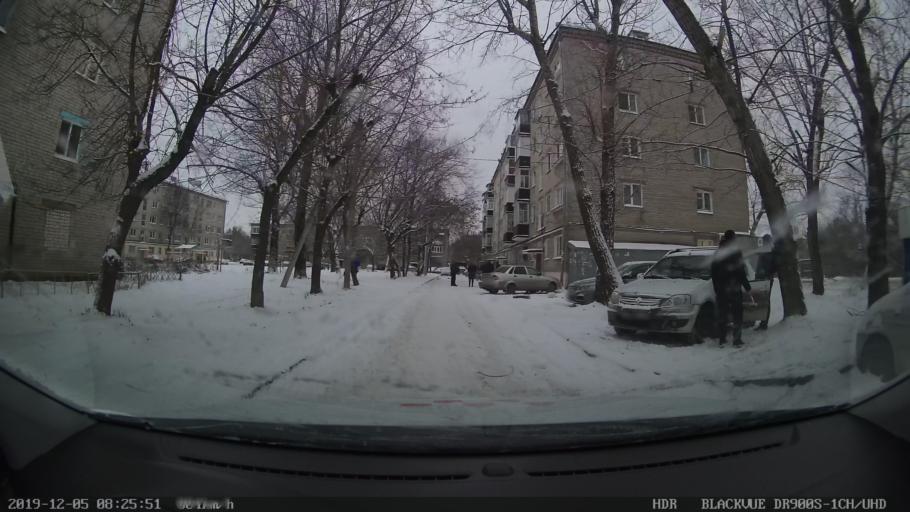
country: RU
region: Tatarstan
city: Staroye Arakchino
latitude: 55.8776
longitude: 49.0232
